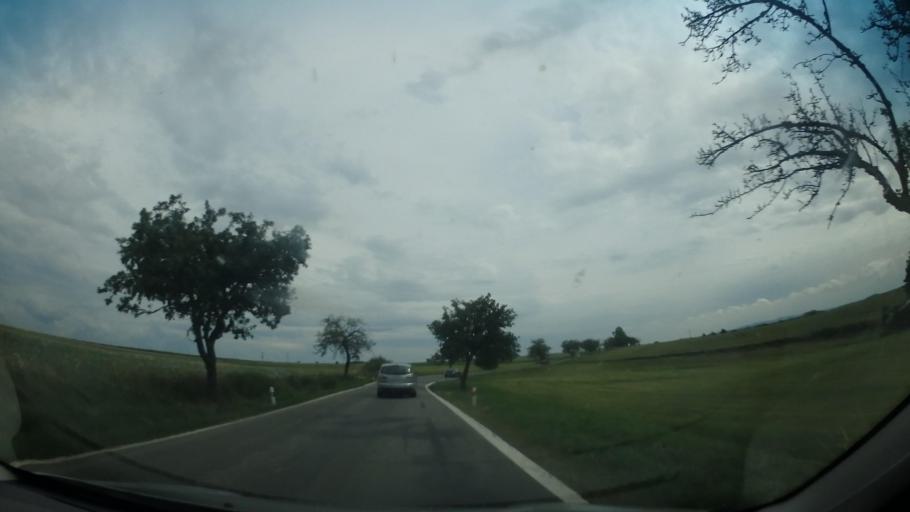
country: CZ
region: Vysocina
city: Bystrice nad Pernstejnem
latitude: 49.5015
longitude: 16.1728
